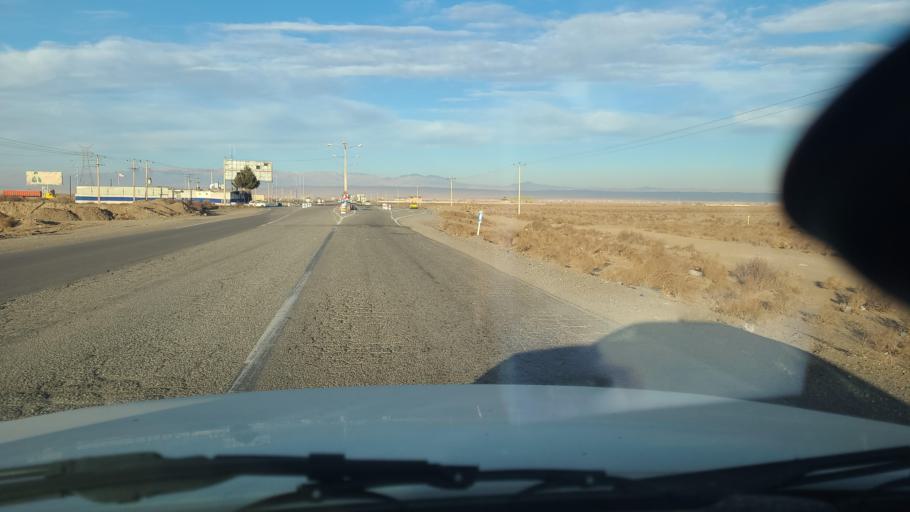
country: IR
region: Razavi Khorasan
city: Neqab
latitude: 36.5833
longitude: 57.5807
